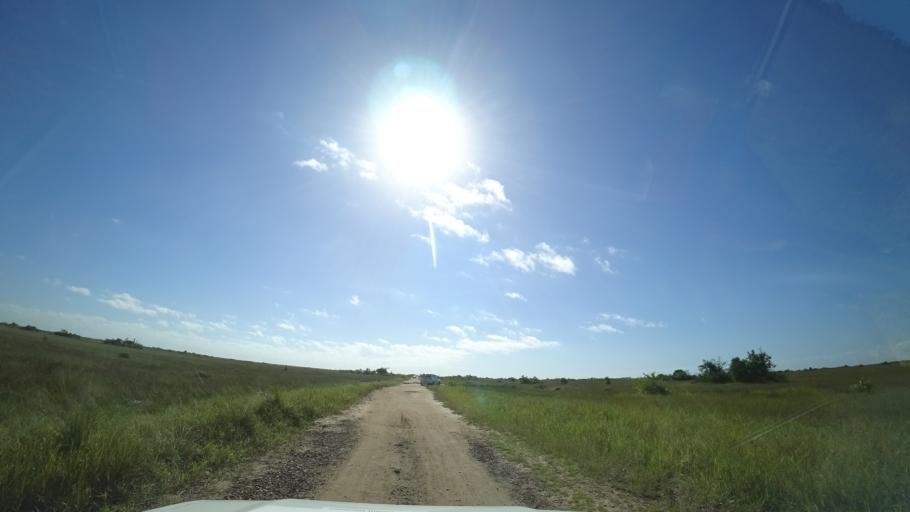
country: MZ
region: Sofala
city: Beira
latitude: -19.7042
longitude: 35.0214
